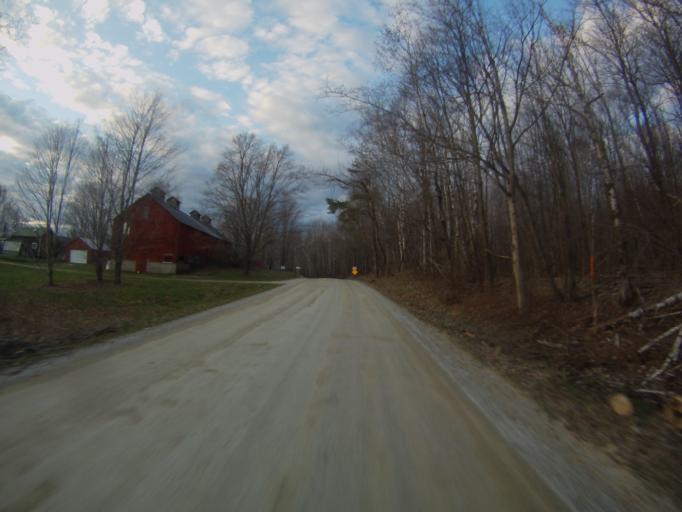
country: US
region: Vermont
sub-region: Rutland County
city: Brandon
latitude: 43.8874
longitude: -73.0100
